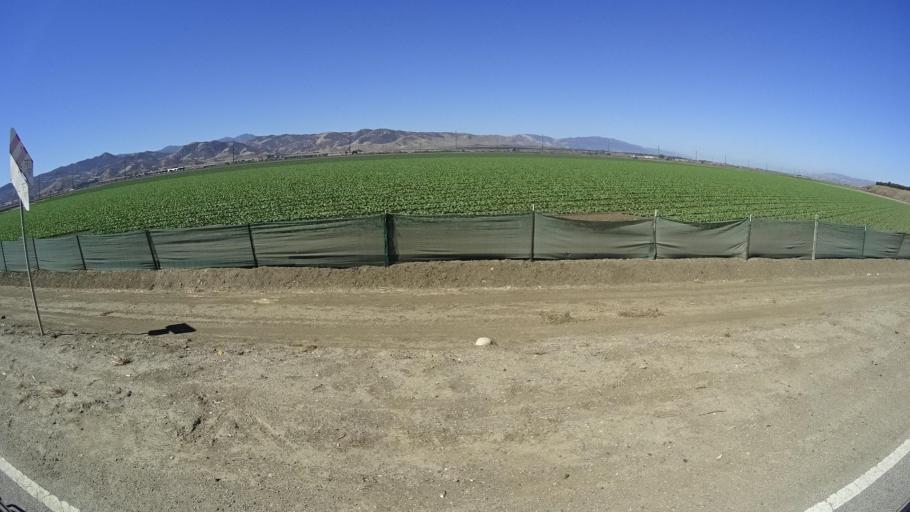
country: US
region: California
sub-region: Monterey County
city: King City
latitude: 36.2347
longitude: -121.1268
